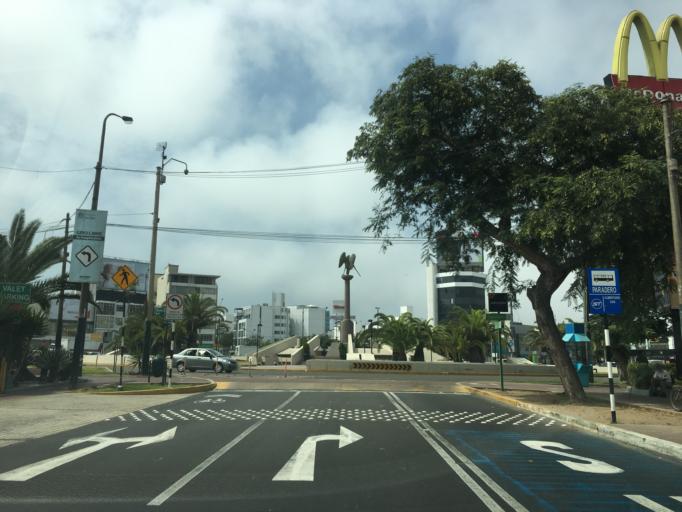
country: PE
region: Lima
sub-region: Lima
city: San Isidro
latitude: -12.1098
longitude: -77.0375
